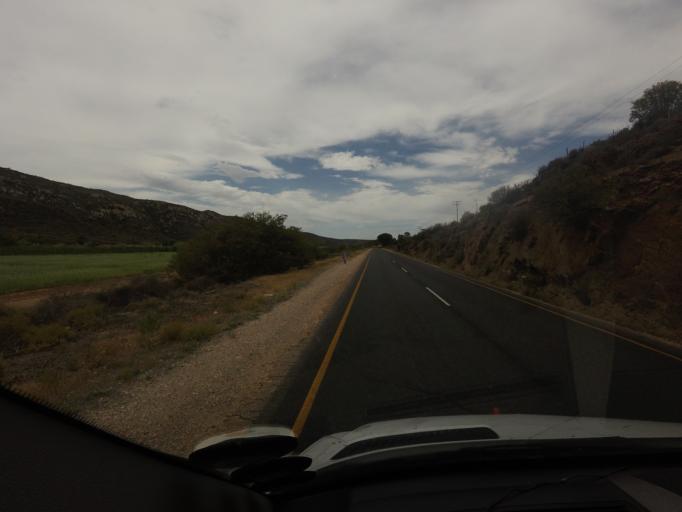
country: ZA
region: Western Cape
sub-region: Overberg District Municipality
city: Swellendam
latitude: -33.8556
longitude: 20.8025
